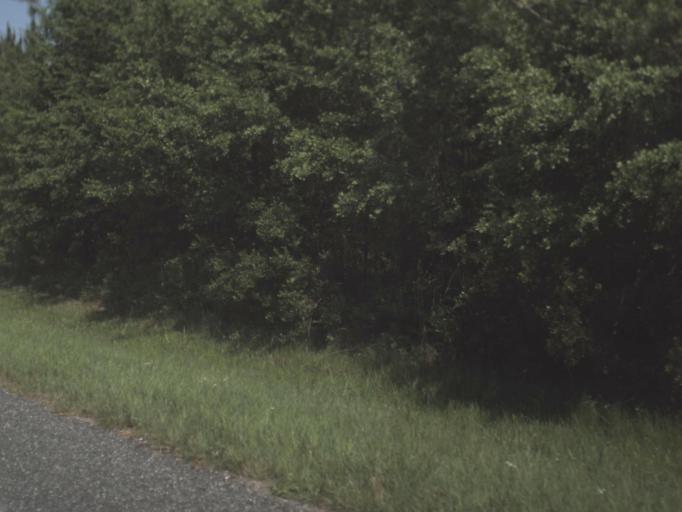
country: US
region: Florida
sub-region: Clay County
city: Middleburg
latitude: 29.9785
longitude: -81.9091
